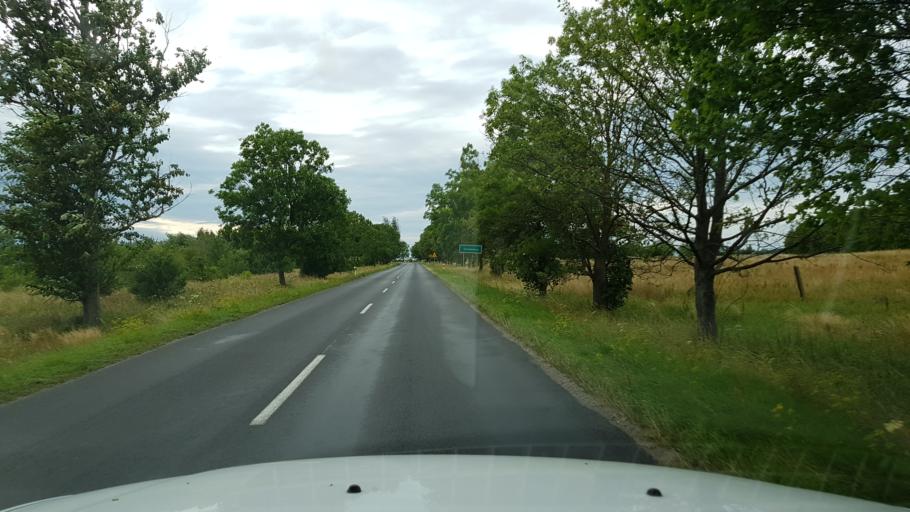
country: PL
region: West Pomeranian Voivodeship
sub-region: Powiat kolobrzeski
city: Kolobrzeg
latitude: 54.1508
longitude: 15.6362
